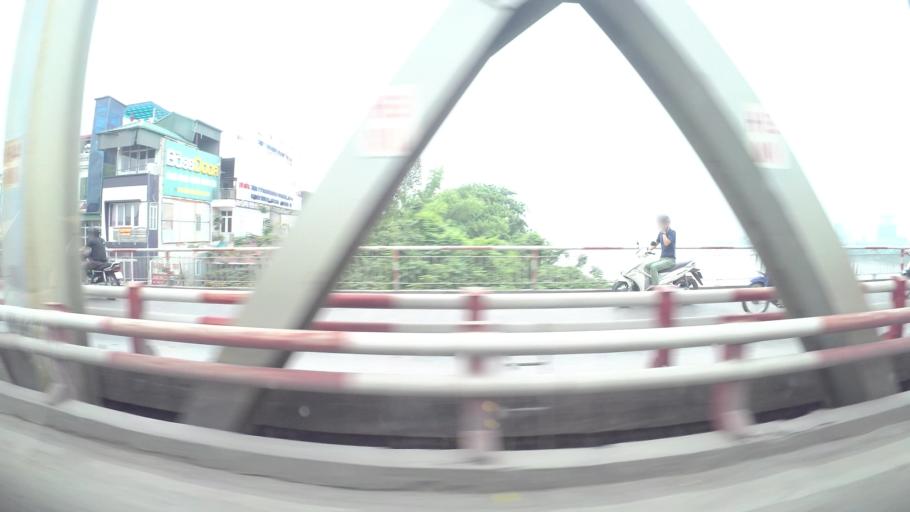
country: VN
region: Ha Noi
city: Hoan Kiem
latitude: 21.0392
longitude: 105.8648
